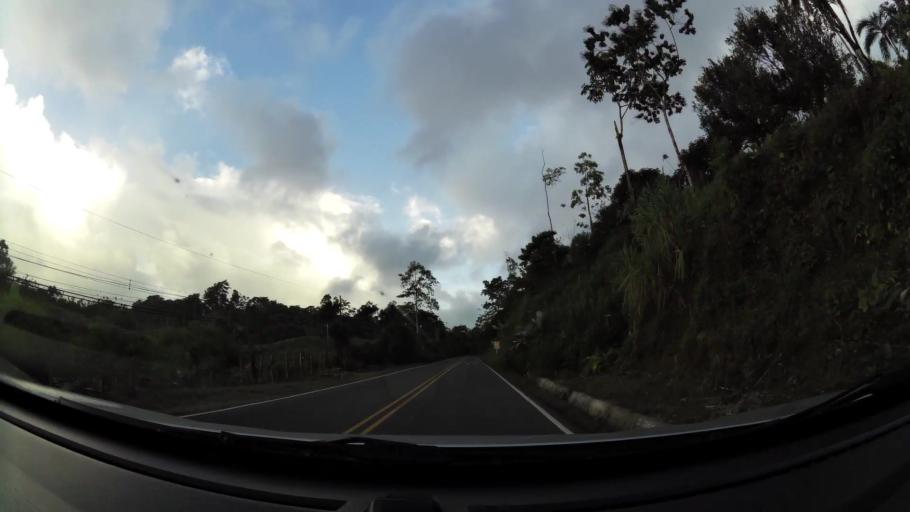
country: CR
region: Limon
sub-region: Canton de Siquirres
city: Siquirres
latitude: 9.9834
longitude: -83.5706
